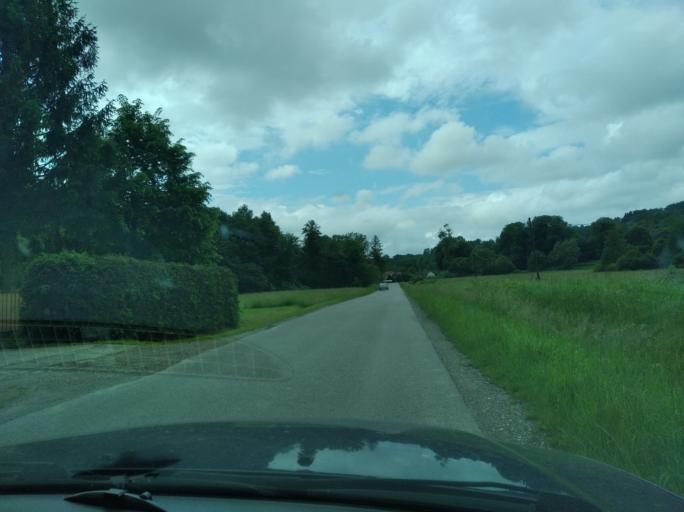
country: PL
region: Subcarpathian Voivodeship
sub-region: Powiat przemyski
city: Dubiecko
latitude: 49.8392
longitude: 22.4016
